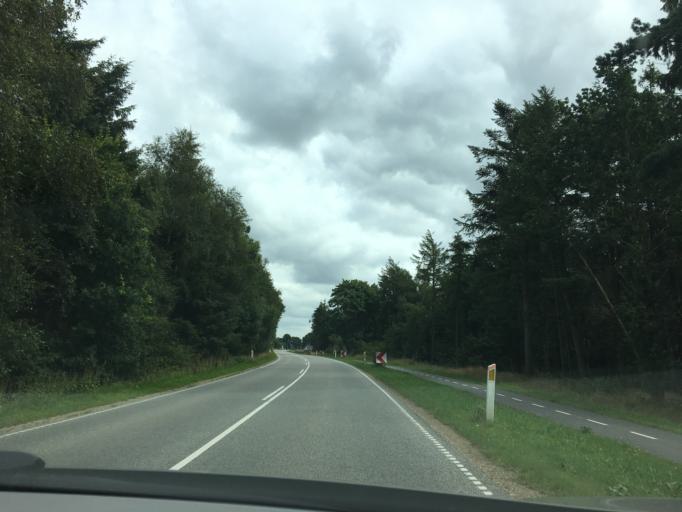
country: DK
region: South Denmark
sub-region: Billund Kommune
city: Grindsted
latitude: 55.8175
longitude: 9.0132
